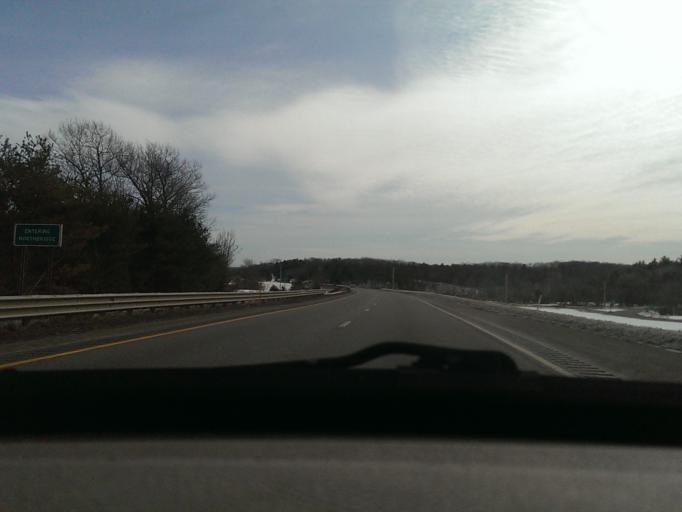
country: US
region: Massachusetts
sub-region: Worcester County
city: East Douglas
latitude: 42.1037
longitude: -71.7054
